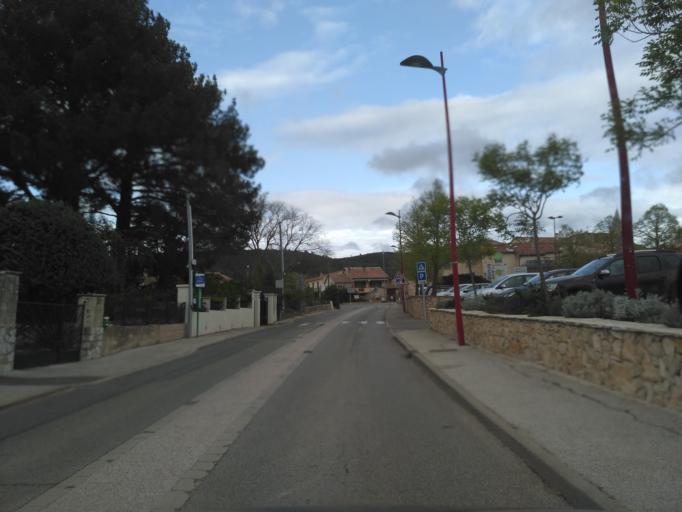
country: FR
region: Provence-Alpes-Cote d'Azur
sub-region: Departement du Var
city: Barjols
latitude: 43.5924
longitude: 6.0138
